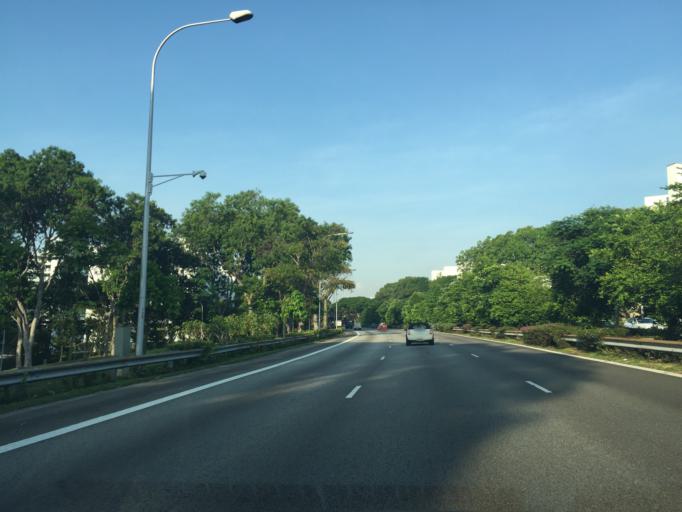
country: SG
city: Singapore
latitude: 1.3497
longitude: 103.9570
